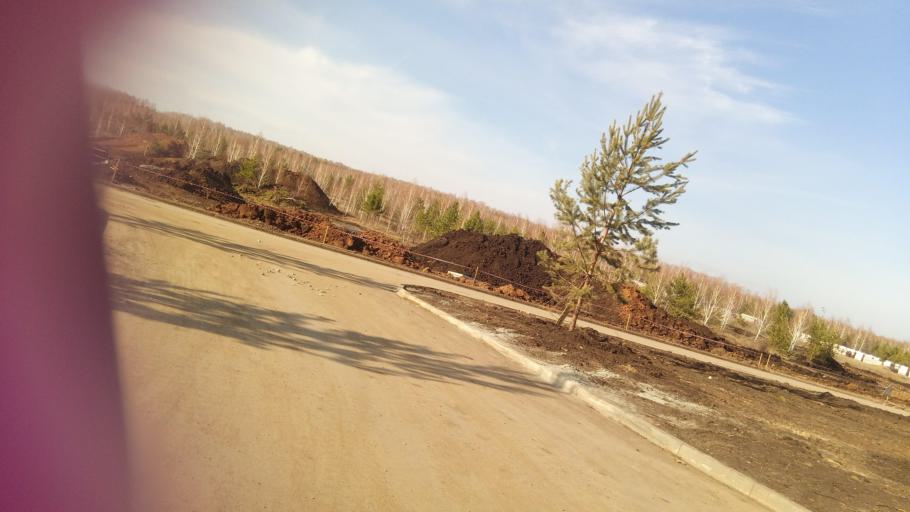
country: RU
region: Chelyabinsk
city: Sargazy
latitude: 55.1129
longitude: 61.2527
